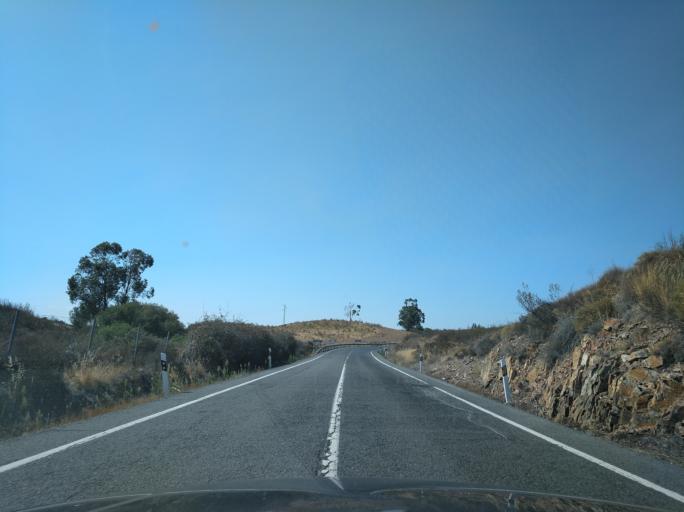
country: ES
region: Andalusia
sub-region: Provincia de Huelva
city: San Bartolome de la Torre
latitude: 37.4835
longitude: -7.1295
